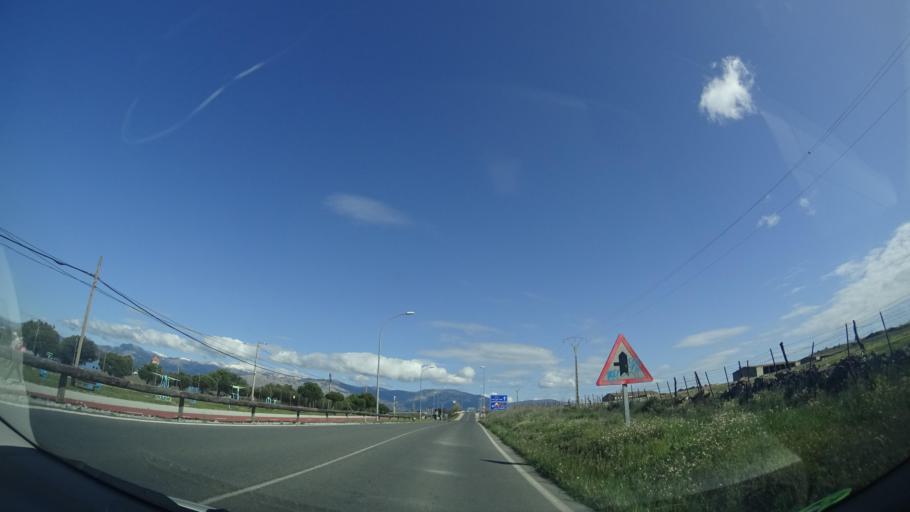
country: ES
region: Madrid
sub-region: Provincia de Madrid
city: Colmenar Viejo
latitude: 40.6816
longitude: -3.7837
